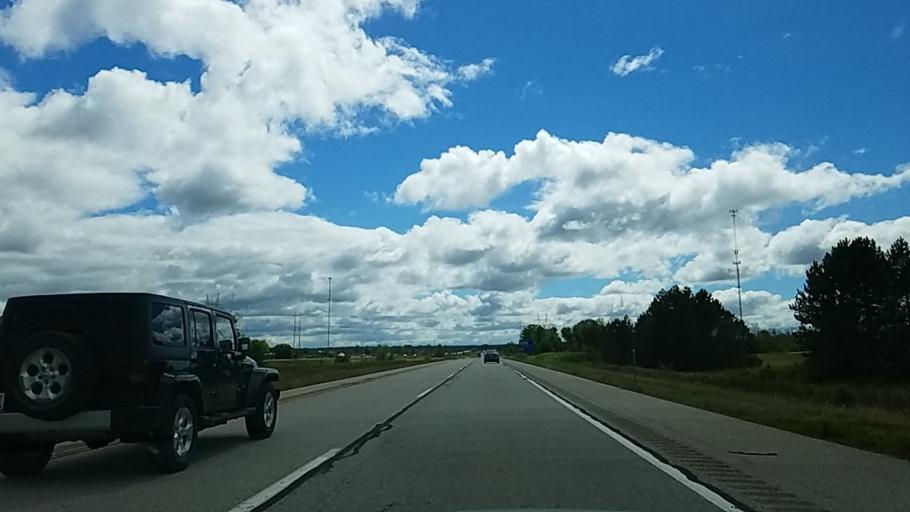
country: US
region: Michigan
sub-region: Ogemaw County
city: Skidway Lake
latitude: 44.1449
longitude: -84.1455
